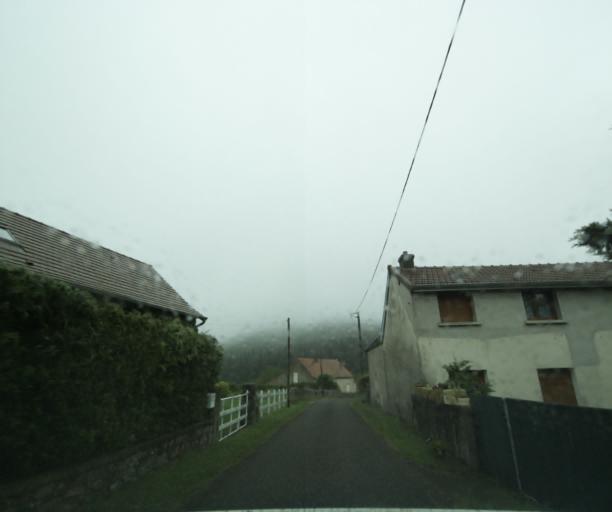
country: FR
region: Bourgogne
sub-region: Departement de Saone-et-Loire
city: Matour
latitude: 46.4039
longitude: 4.4061
